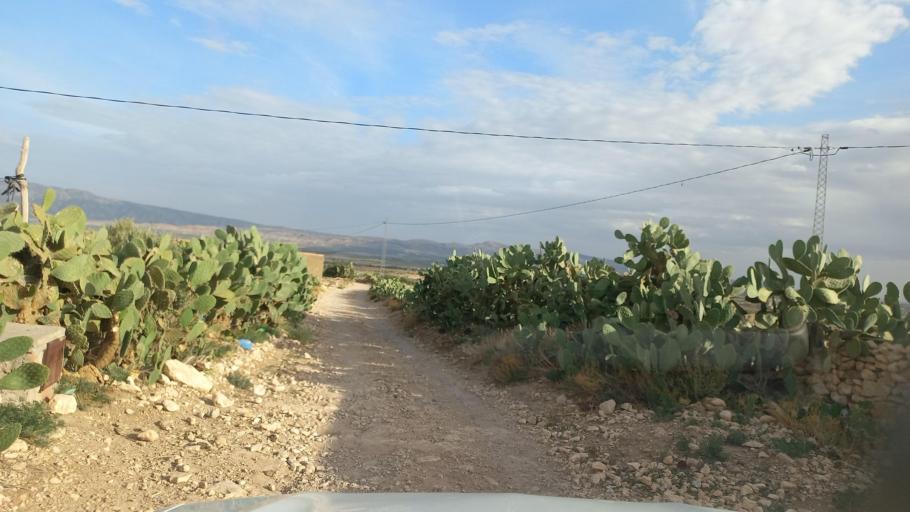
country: TN
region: Al Qasrayn
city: Sbiba
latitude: 35.4551
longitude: 9.0791
